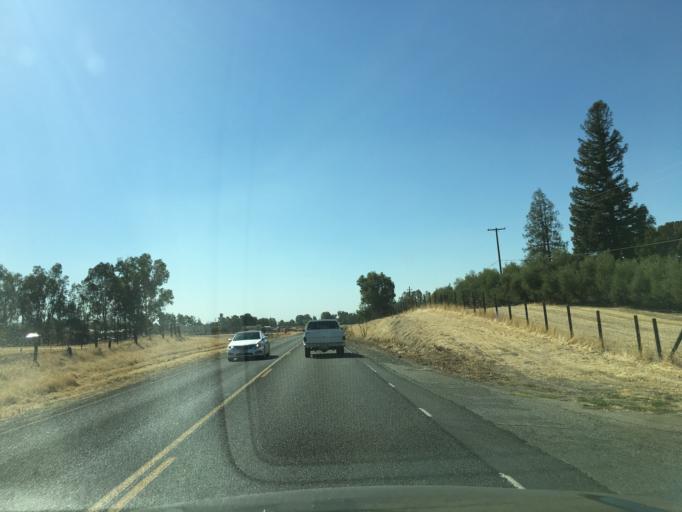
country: US
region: California
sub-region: Madera County
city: Parksdale
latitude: 36.9991
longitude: -119.9767
